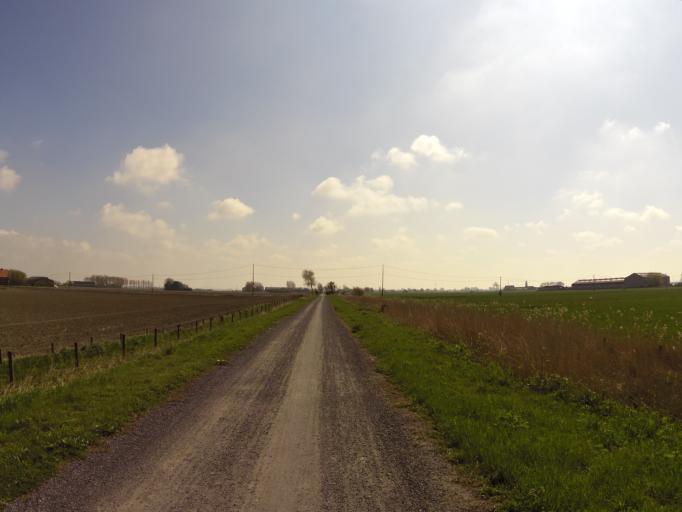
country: BE
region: Flanders
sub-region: Provincie West-Vlaanderen
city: Nieuwpoort
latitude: 51.1026
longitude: 2.7745
